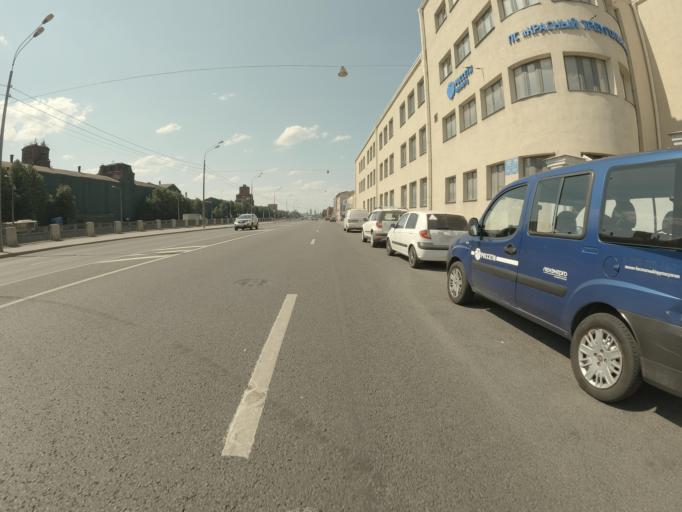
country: RU
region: St.-Petersburg
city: Admiralteisky
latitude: 59.9093
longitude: 30.2916
